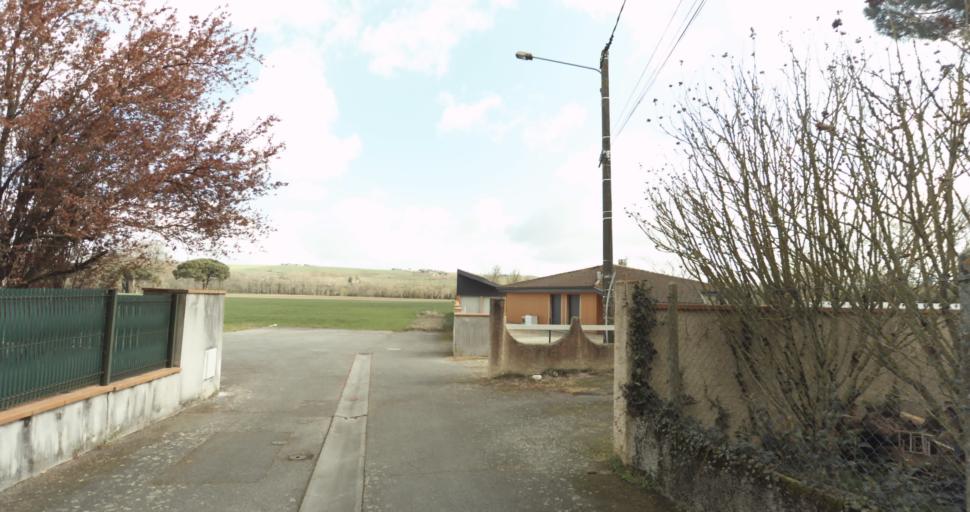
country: FR
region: Midi-Pyrenees
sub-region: Departement de la Haute-Garonne
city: Auterive
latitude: 43.3589
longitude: 1.4670
